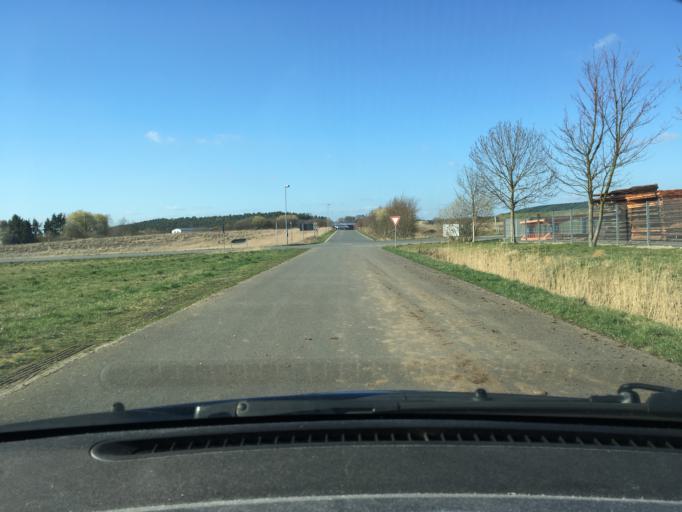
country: DE
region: Lower Saxony
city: Dahlem
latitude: 53.1900
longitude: 10.7504
